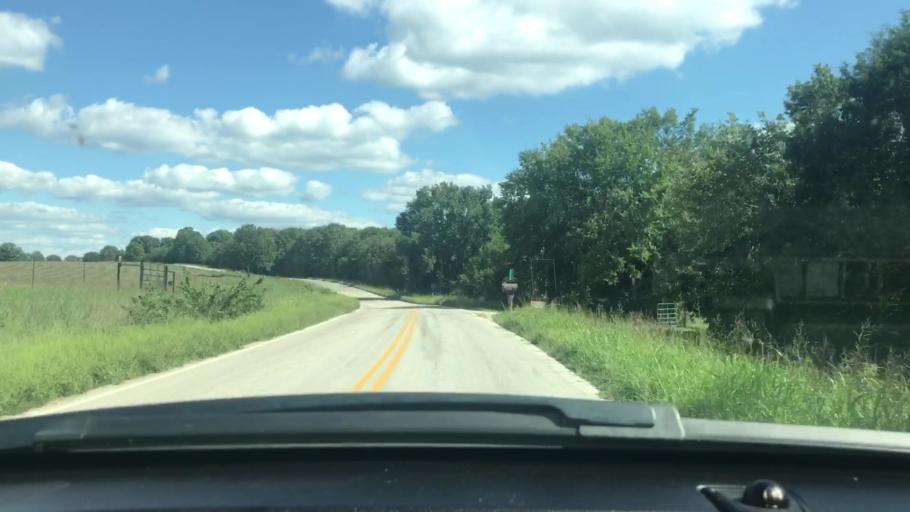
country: US
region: Missouri
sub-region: Wright County
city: Hartville
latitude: 37.3784
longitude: -92.4344
